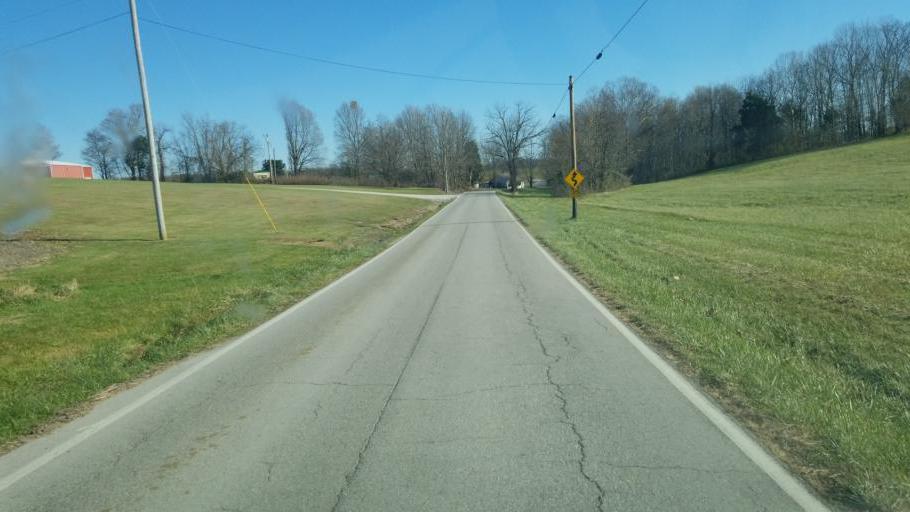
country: US
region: Ohio
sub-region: Adams County
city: Manchester
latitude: 38.5333
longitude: -83.6241
